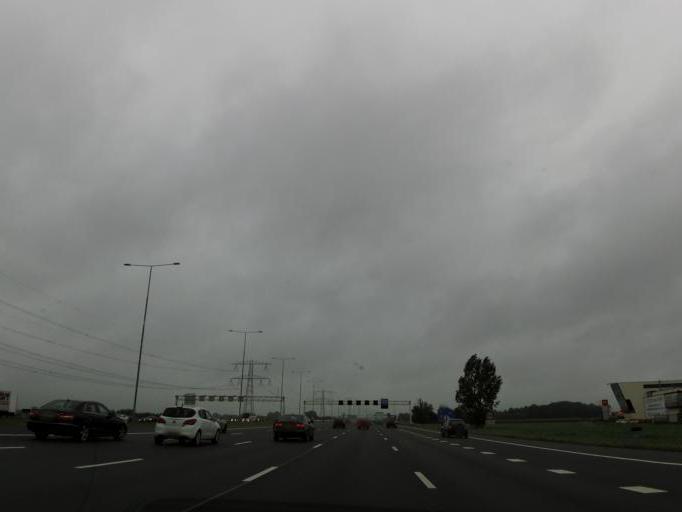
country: NL
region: Utrecht
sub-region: Stichtse Vecht
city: Breukelen
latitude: 52.1783
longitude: 4.9870
